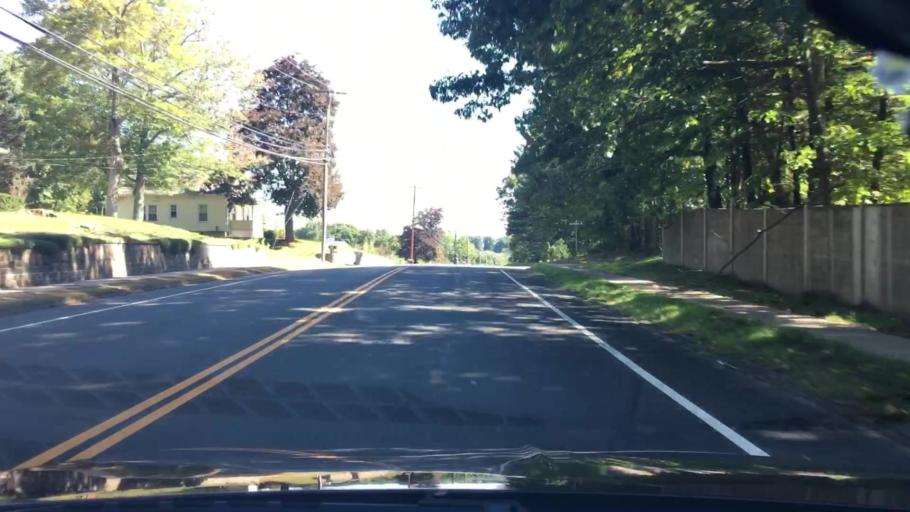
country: US
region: Connecticut
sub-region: Hartford County
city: Bristol
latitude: 41.7036
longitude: -72.9503
